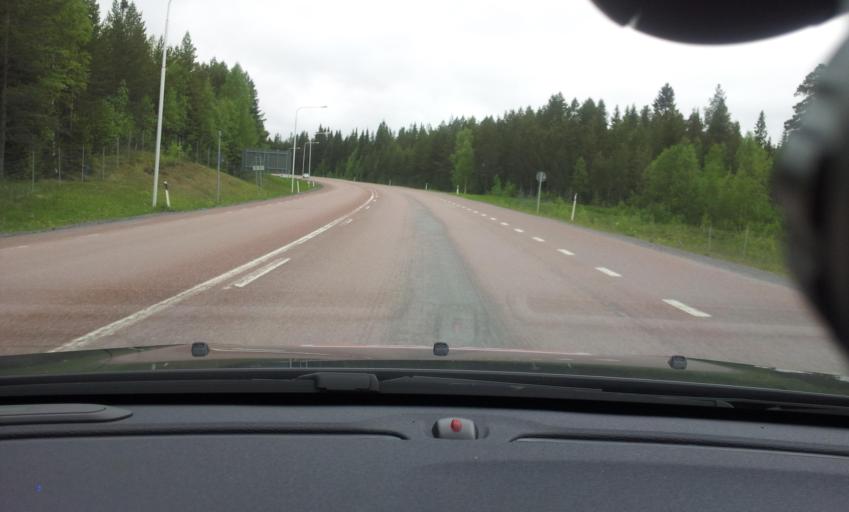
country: SE
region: Jaemtland
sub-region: Krokoms Kommun
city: Krokom
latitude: 63.3287
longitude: 14.4260
